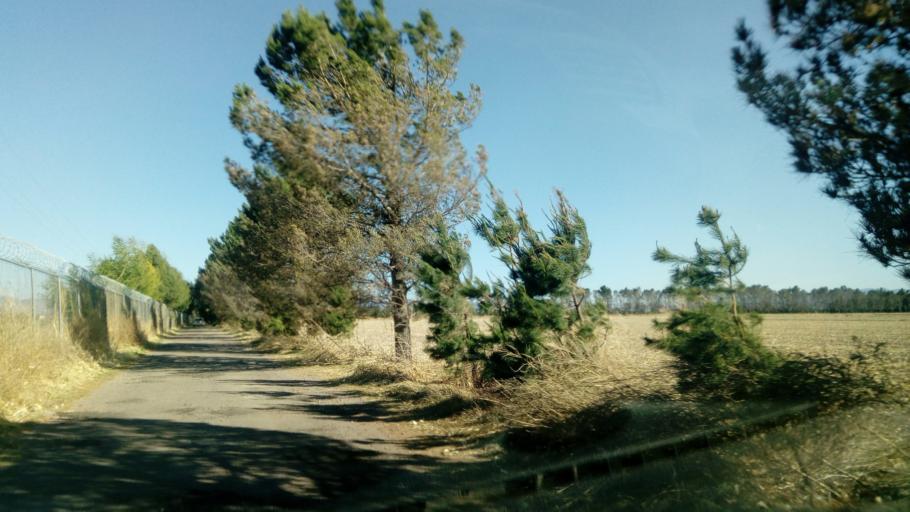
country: MX
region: Durango
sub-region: Durango
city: Jose Refugio Salcido
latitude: 24.0128
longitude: -104.5541
